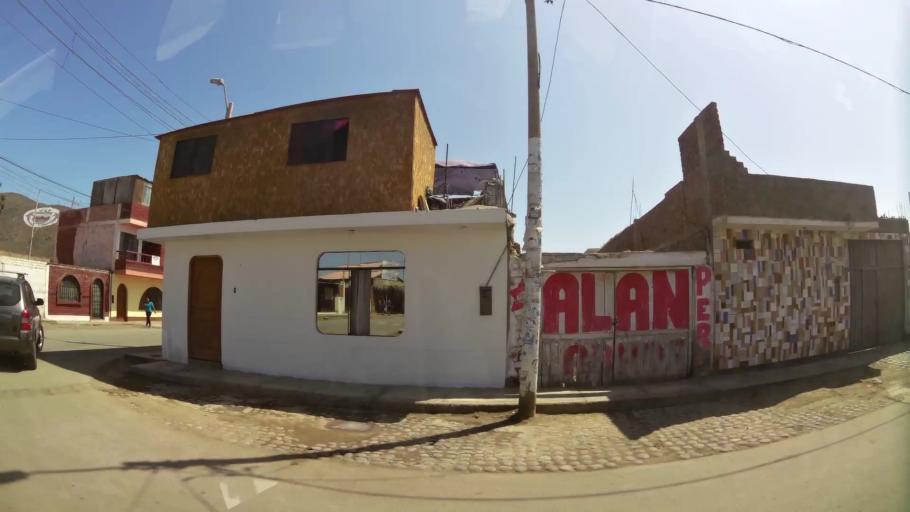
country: PE
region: Lima
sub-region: Provincia de Canete
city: San Vicente de Canete
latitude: -13.0286
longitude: -76.4810
